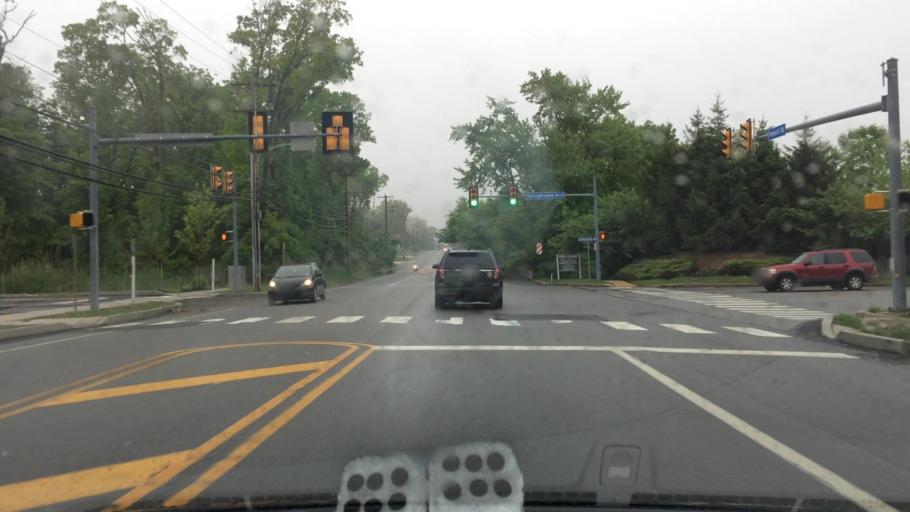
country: US
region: Pennsylvania
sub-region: Delaware County
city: Village Green-Green Ridge
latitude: 39.8533
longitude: -75.4266
